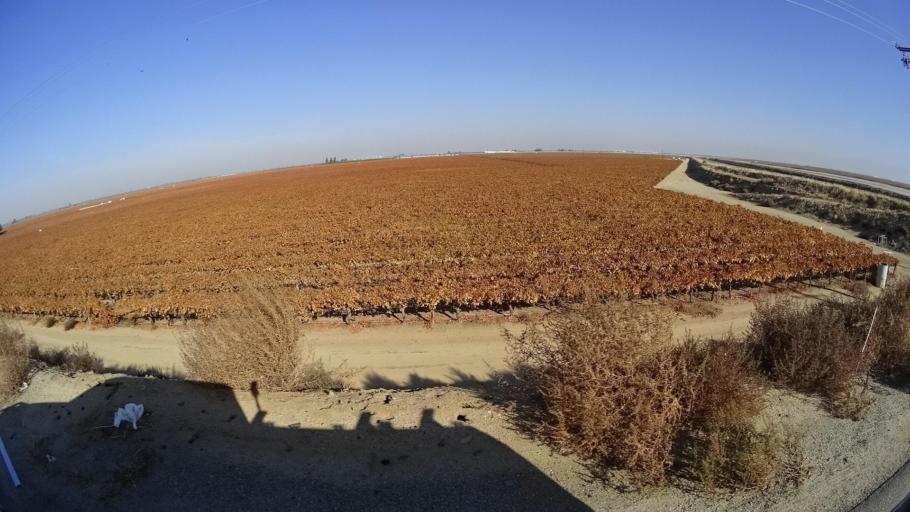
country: US
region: California
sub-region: Kern County
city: Delano
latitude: 35.7469
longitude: -119.1832
